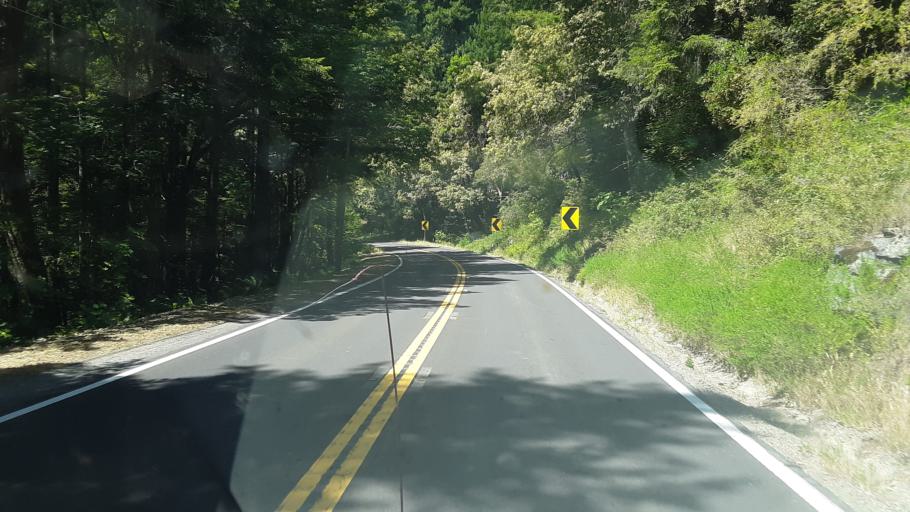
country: US
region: California
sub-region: Del Norte County
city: Bertsch-Oceanview
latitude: 41.8089
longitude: -124.0506
